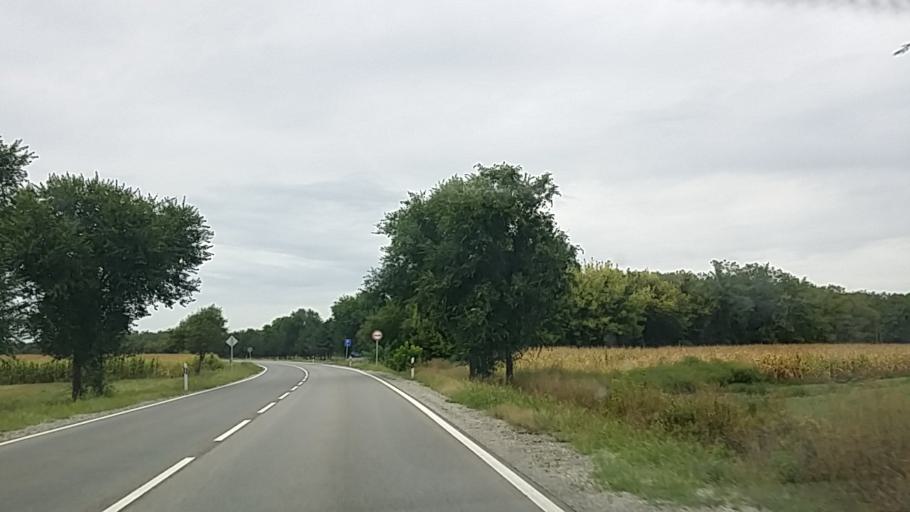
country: HU
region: Gyor-Moson-Sopron
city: Fertoszentmiklos
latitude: 47.5958
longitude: 16.8346
